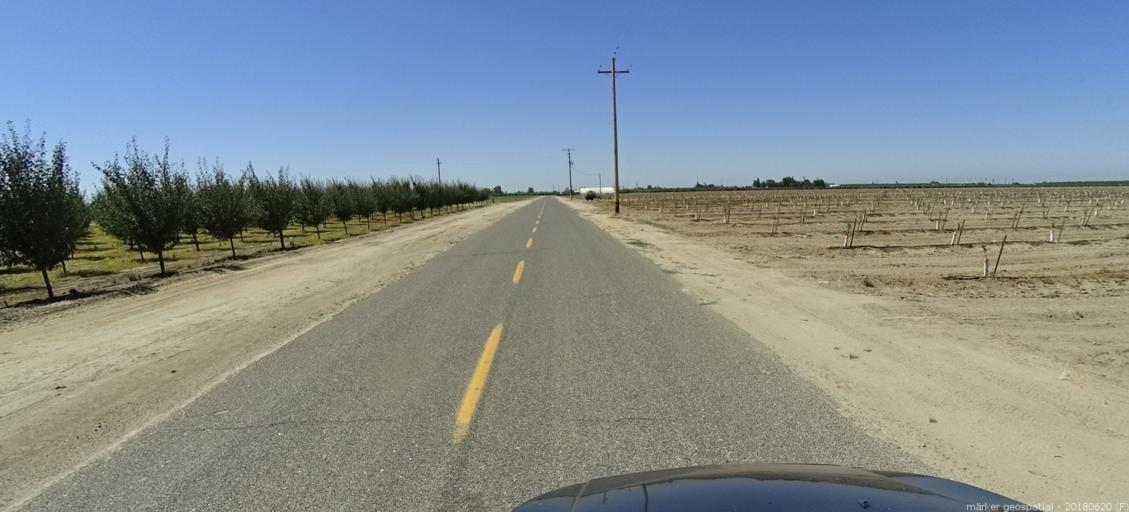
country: US
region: California
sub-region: Fresno County
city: Biola
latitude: 36.8416
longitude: -120.0192
